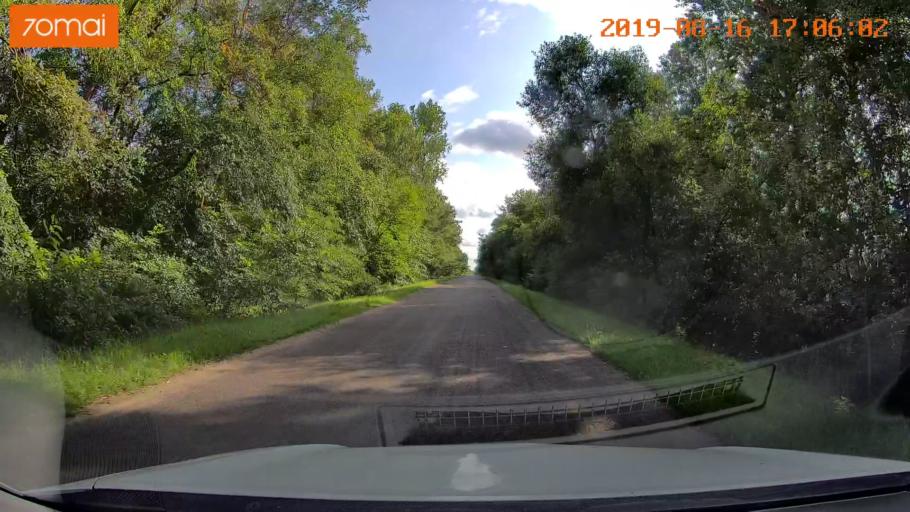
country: BY
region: Mogilev
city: Hlusha
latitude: 53.2312
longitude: 28.9376
